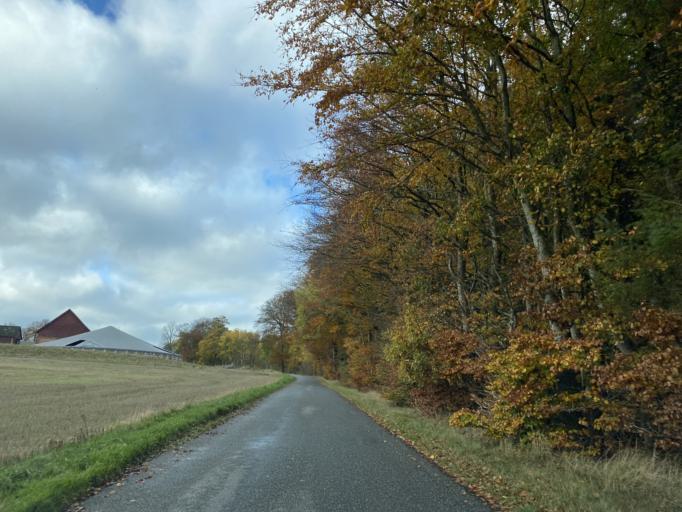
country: DK
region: Central Jutland
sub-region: Skanderborg Kommune
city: Galten
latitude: 56.2181
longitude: 9.9366
